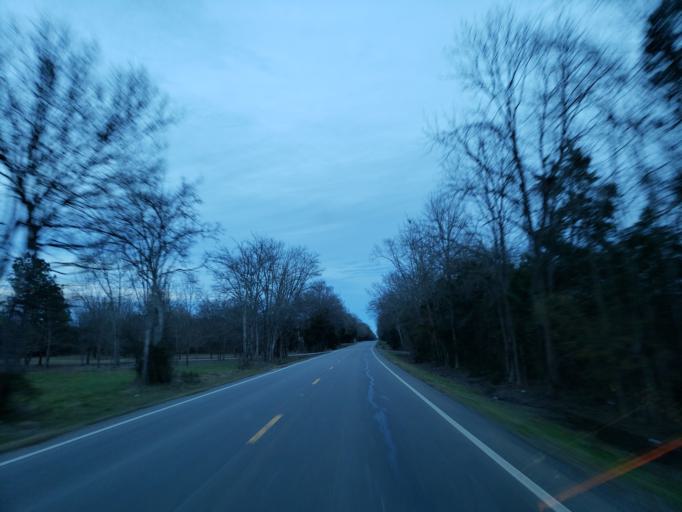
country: US
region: Alabama
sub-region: Sumter County
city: Livingston
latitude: 32.8114
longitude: -88.2477
